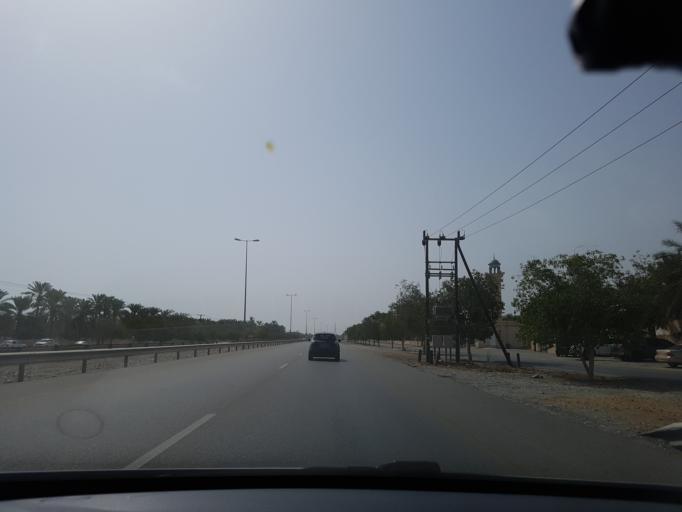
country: OM
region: Al Batinah
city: Al Khaburah
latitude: 23.9861
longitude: 57.0764
